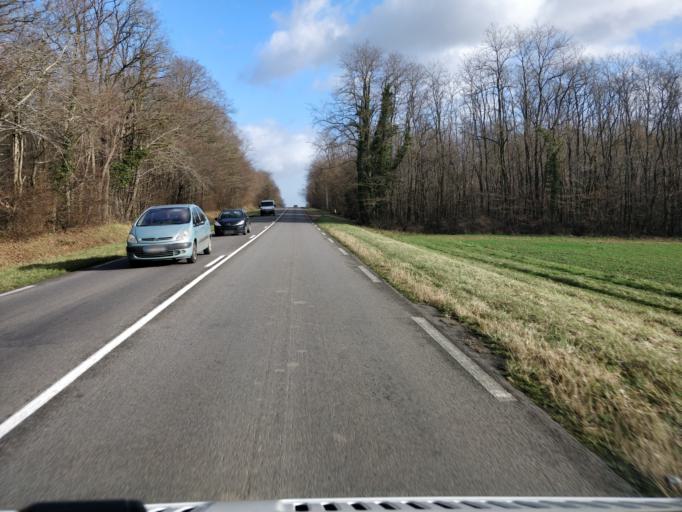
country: FR
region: Bourgogne
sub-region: Departement de l'Yonne
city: Paron
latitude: 48.1795
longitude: 3.2059
